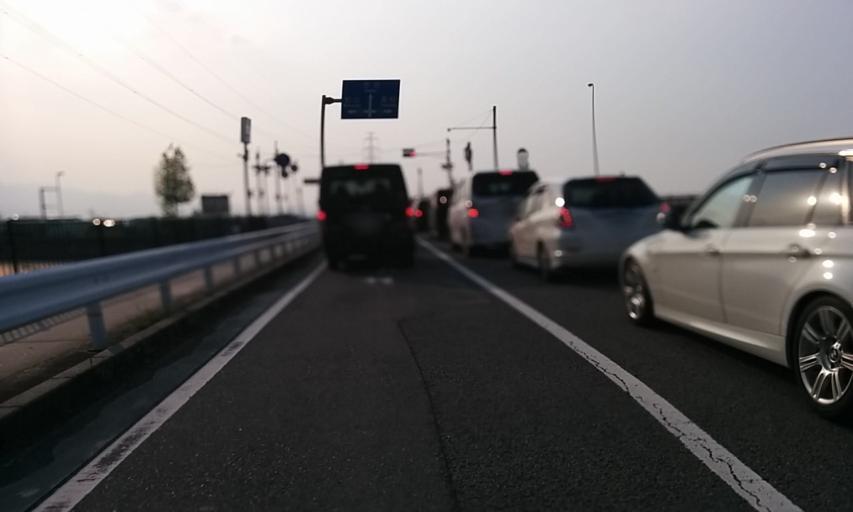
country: JP
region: Ehime
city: Saijo
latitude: 33.9020
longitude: 133.1841
